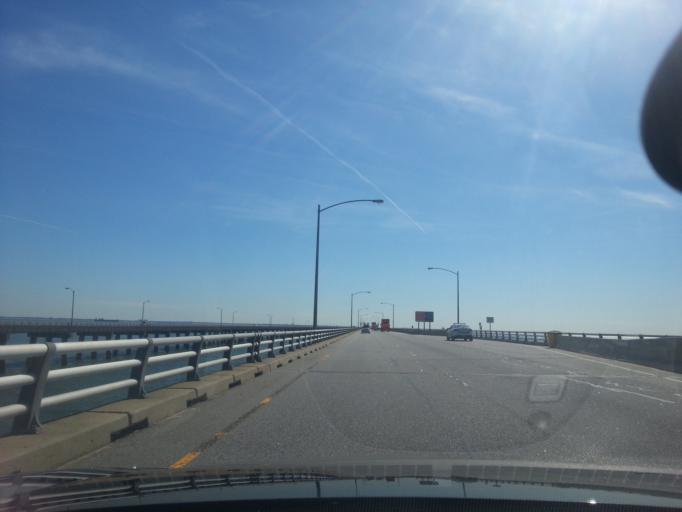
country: US
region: Virginia
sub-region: City of Virginia Beach
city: Virginia Beach
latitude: 37.0108
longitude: -76.0951
